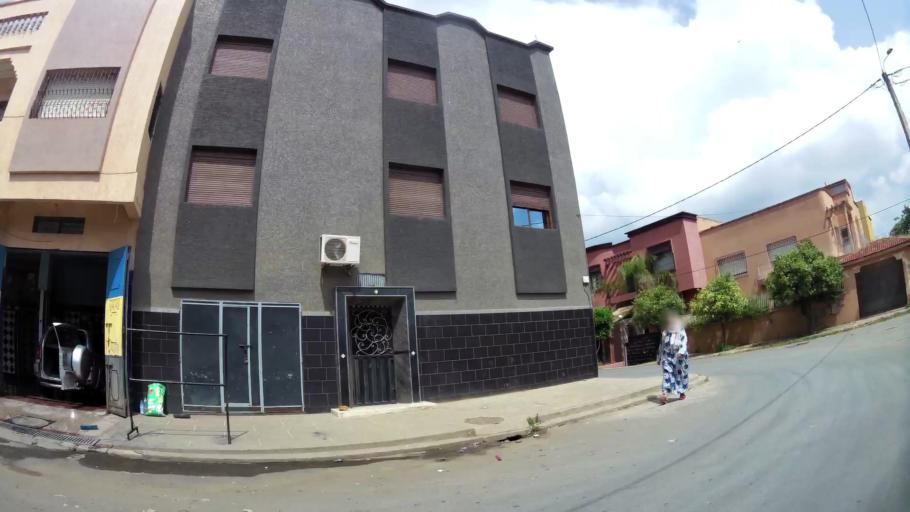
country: MA
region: Rabat-Sale-Zemmour-Zaer
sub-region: Khemisset
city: Tiflet
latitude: 33.8934
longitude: -6.3317
